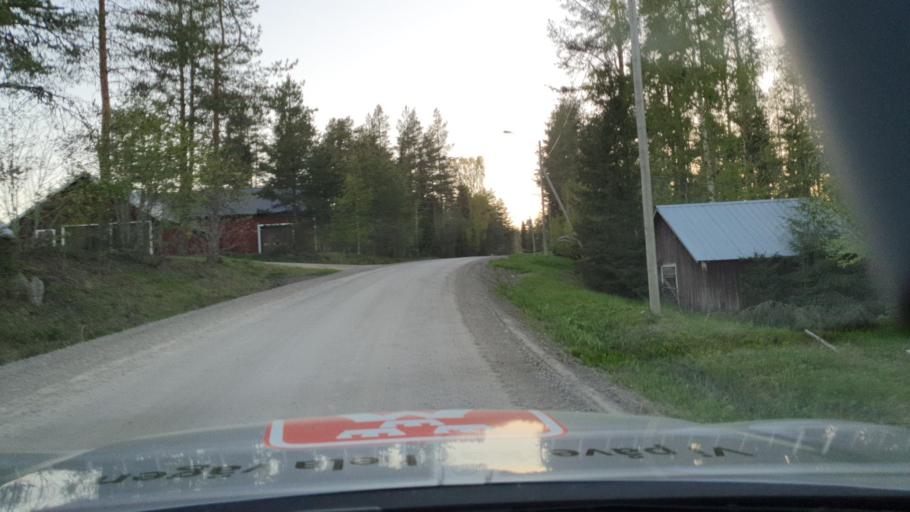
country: SE
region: Vaesternorrland
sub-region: OErnskoeldsviks Kommun
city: Ornskoldsvik
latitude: 63.5271
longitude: 18.5796
